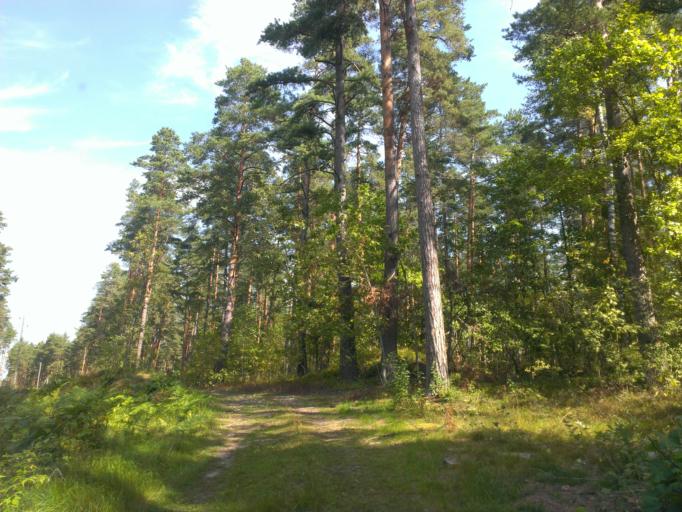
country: LV
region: Adazi
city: Adazi
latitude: 57.0865
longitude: 24.3410
